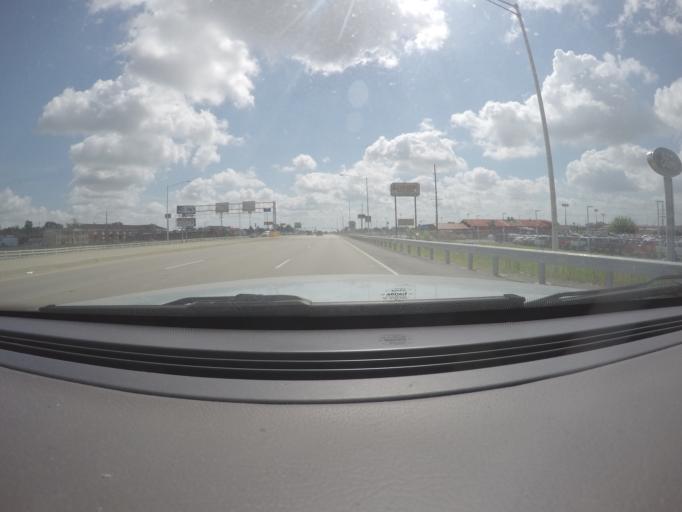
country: US
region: Illinois
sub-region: Williamson County
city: Marion
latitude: 37.7406
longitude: -88.9525
